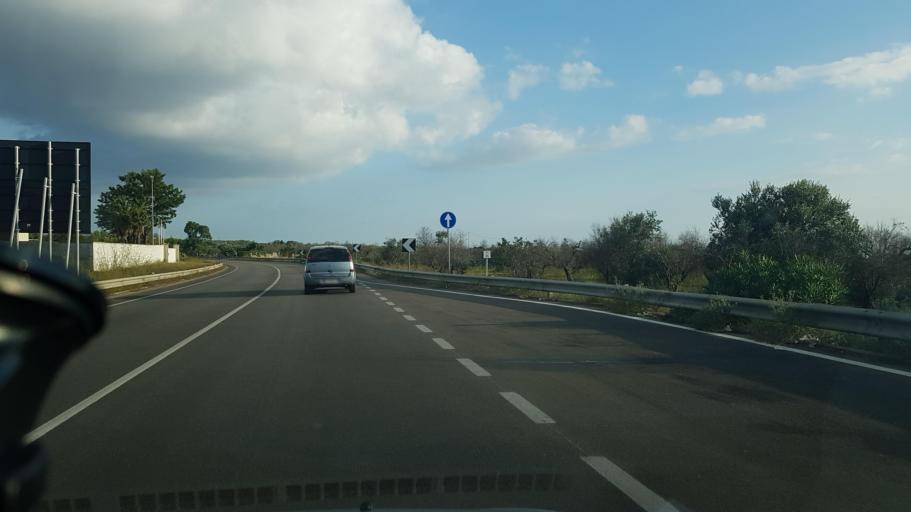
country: IT
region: Apulia
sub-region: Provincia di Lecce
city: Acquarica del Capo
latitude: 39.9100
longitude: 18.2342
